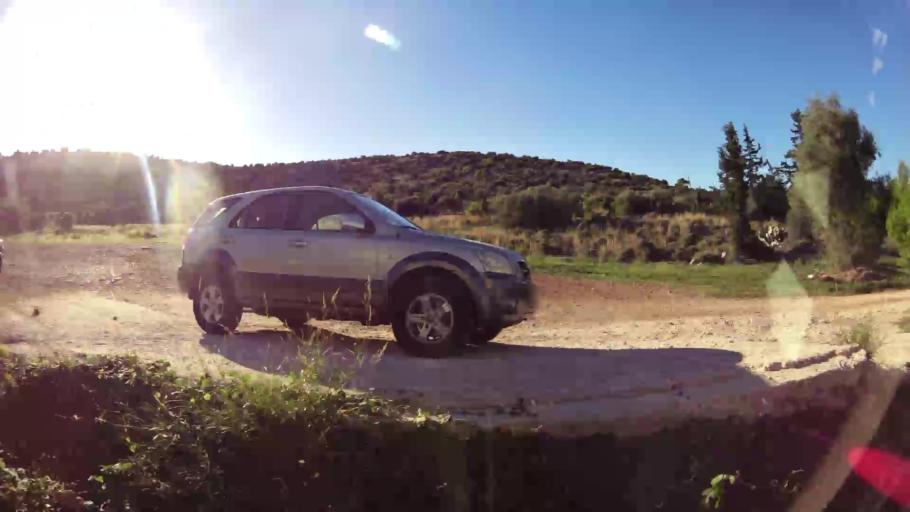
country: GR
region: Attica
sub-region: Nomarchia Anatolikis Attikis
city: Vari
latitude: 37.8315
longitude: 23.7999
